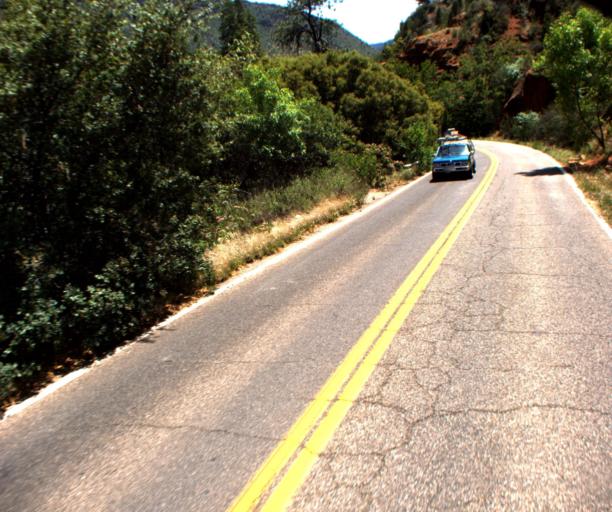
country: US
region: Arizona
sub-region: Coconino County
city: Sedona
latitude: 34.9162
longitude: -111.7302
